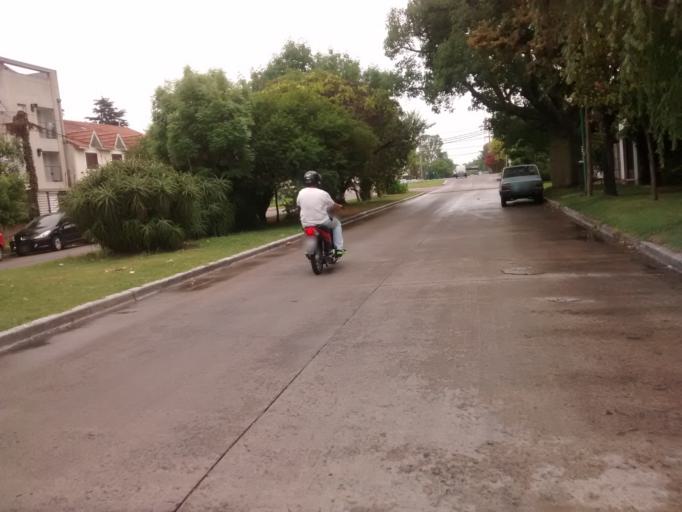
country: AR
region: Buenos Aires
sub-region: Partido de La Plata
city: La Plata
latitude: -34.8997
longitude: -57.9803
